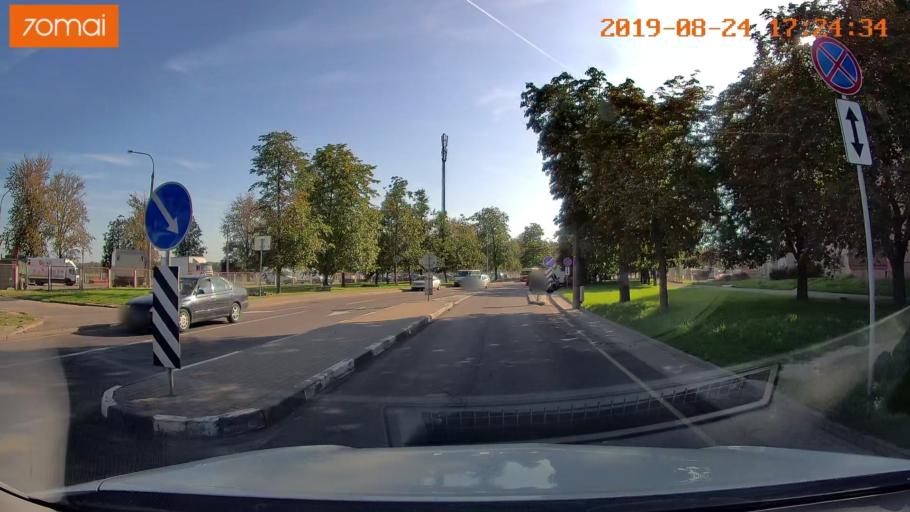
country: BY
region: Minsk
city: Hatava
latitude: 53.8369
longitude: 27.6524
